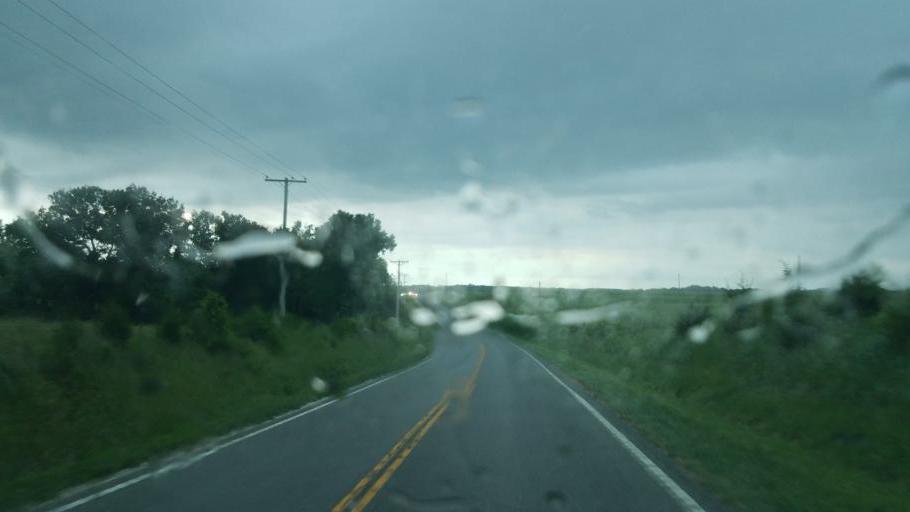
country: US
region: Missouri
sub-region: Cooper County
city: Boonville
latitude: 38.9118
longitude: -92.6821
